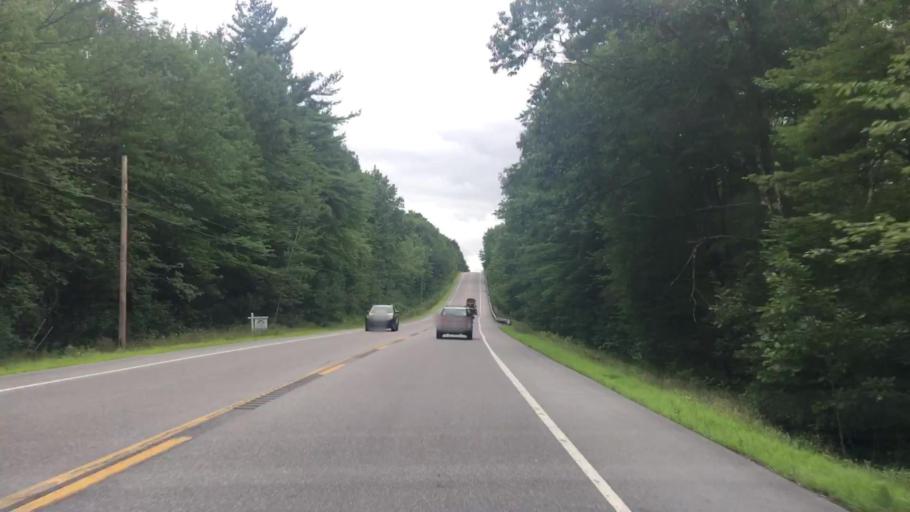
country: US
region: Maine
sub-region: York County
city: Waterboro
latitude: 43.5071
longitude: -70.7168
